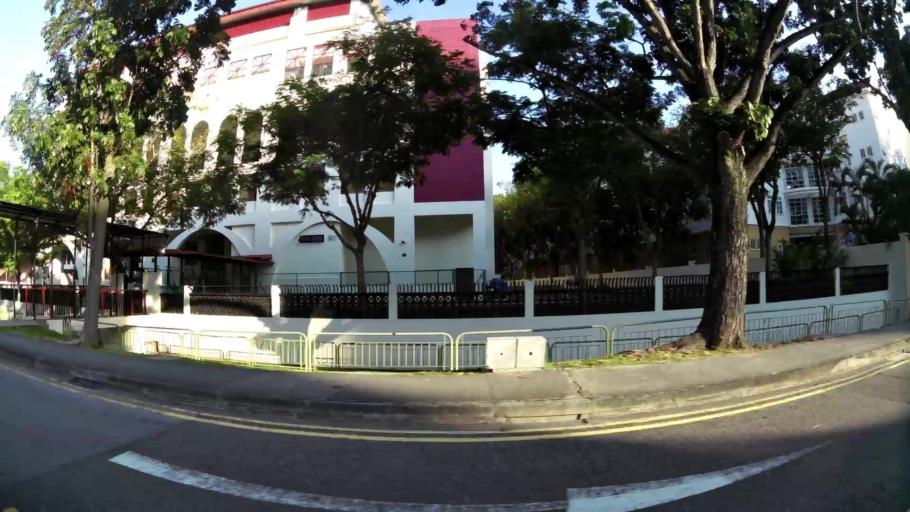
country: SG
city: Singapore
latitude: 1.3060
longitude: 103.9114
